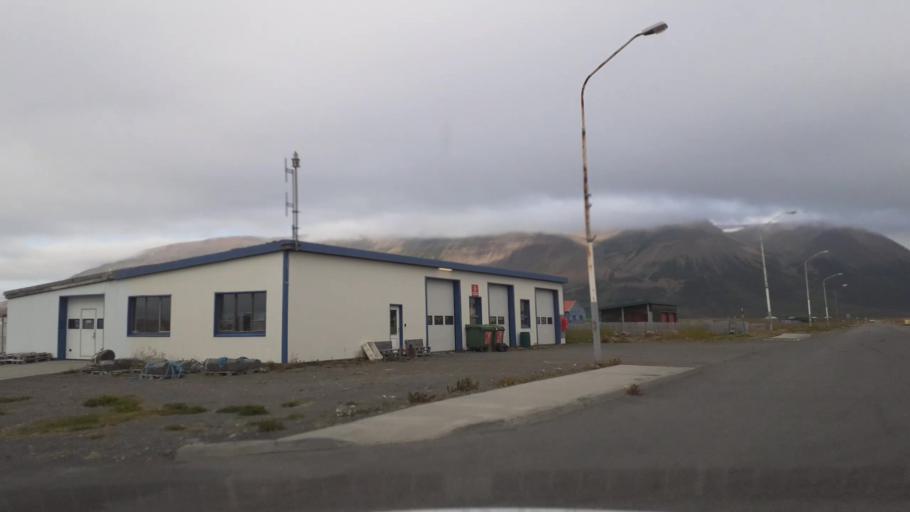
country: IS
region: Northwest
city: Saudarkrokur
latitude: 65.8979
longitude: -19.4109
